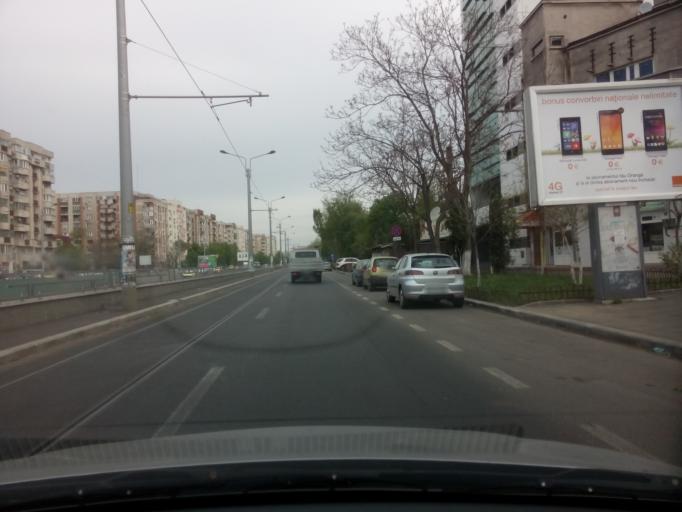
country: RO
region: Bucuresti
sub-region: Municipiul Bucuresti
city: Bucharest
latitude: 44.4327
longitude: 26.1387
